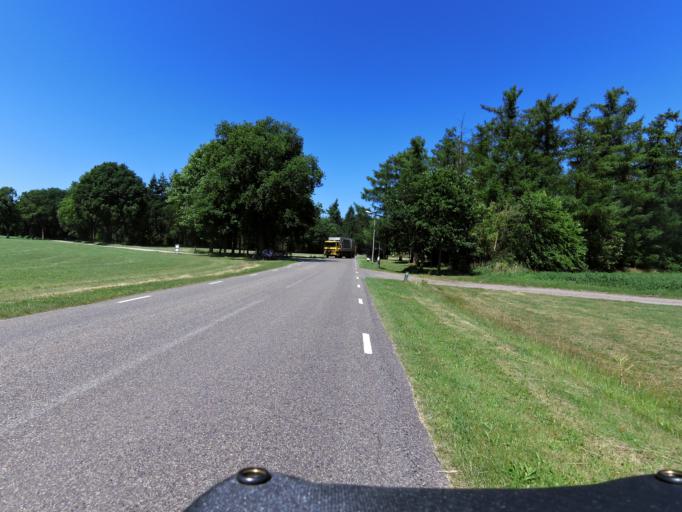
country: NL
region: Overijssel
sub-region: Gemeente Twenterand
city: Magele
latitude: 52.4919
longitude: 6.5083
